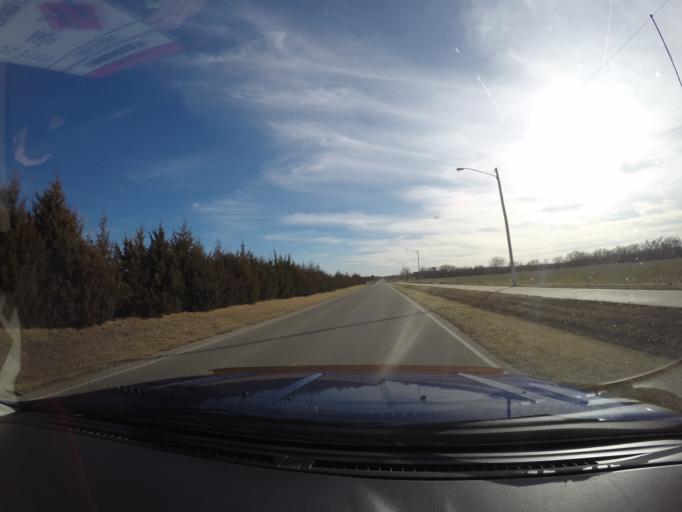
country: US
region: Kansas
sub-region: Harvey County
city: North Newton
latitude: 38.0688
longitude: -97.3369
